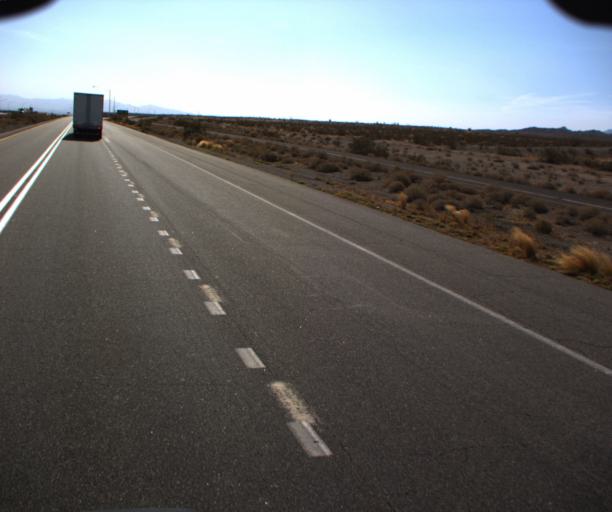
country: US
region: Arizona
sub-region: Mohave County
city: Desert Hills
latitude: 34.7227
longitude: -114.4293
